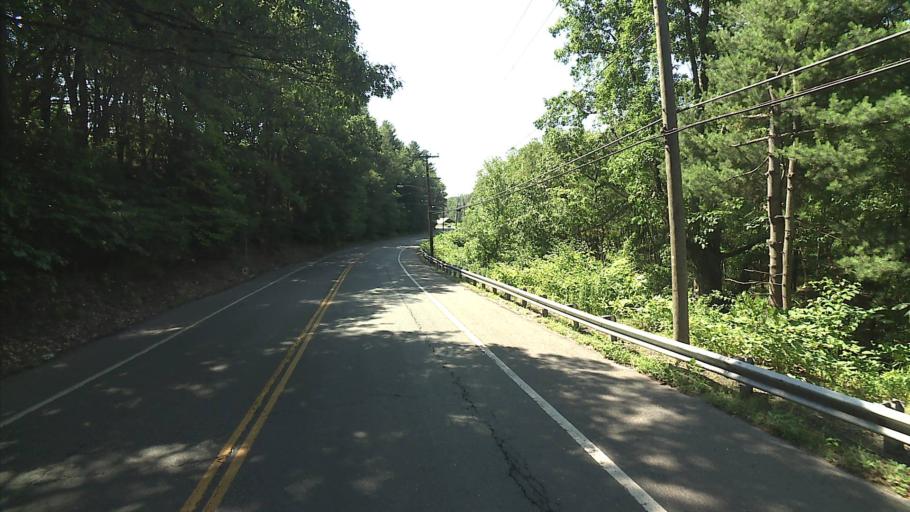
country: US
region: Connecticut
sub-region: Litchfield County
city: Terryville
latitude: 41.6767
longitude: -72.9997
